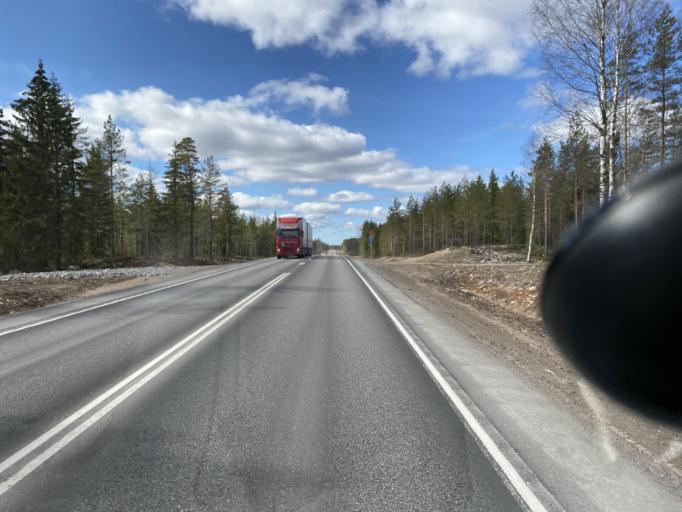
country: FI
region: Satakunta
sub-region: Pori
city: Kokemaeki
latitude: 61.1663
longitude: 22.3977
